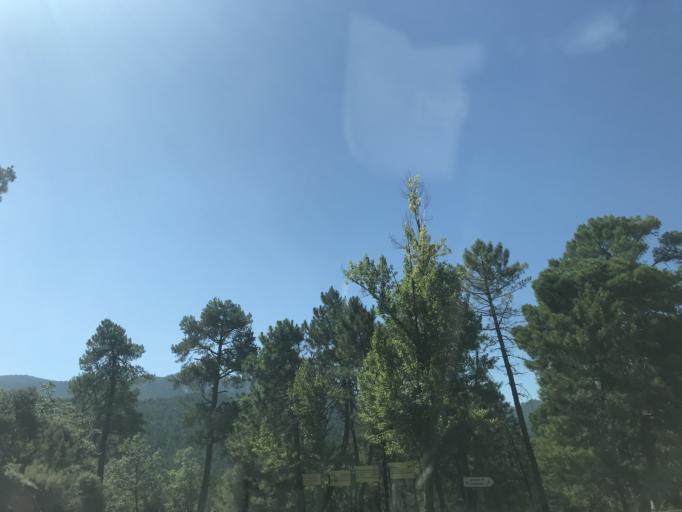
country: ES
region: Andalusia
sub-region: Provincia de Jaen
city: La Iruela
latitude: 37.9206
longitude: -2.9329
